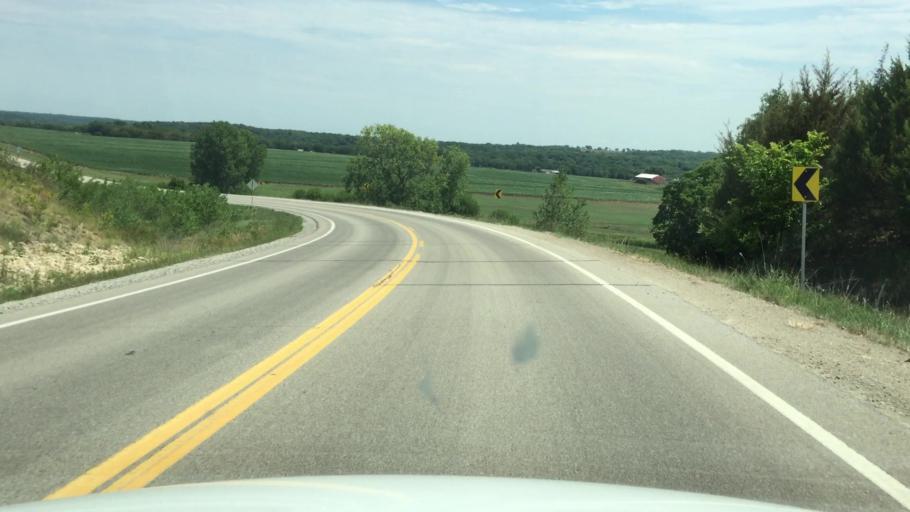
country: US
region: Kansas
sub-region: Osage County
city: Overbrook
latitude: 38.9718
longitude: -95.4905
